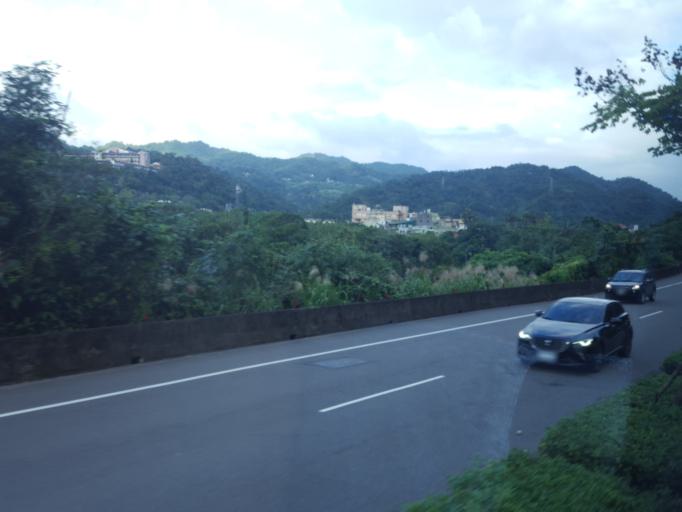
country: TW
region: Taipei
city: Taipei
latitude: 25.0080
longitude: 121.6376
